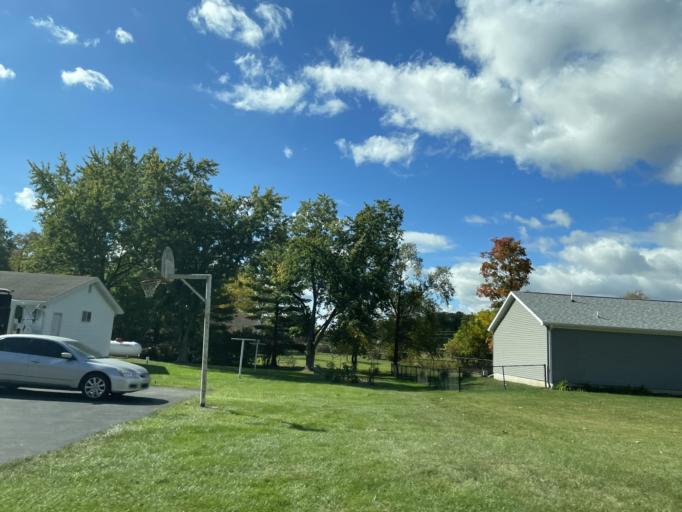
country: US
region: Indiana
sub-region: Allen County
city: Fort Wayne
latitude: 41.1075
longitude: -85.2154
